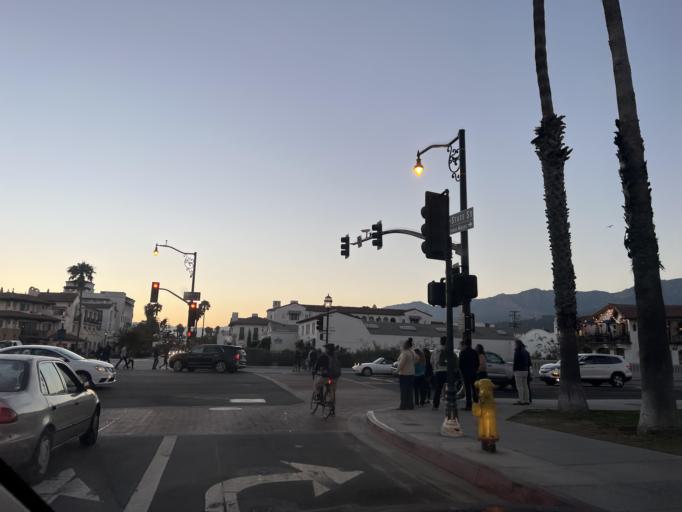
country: US
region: California
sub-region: Santa Barbara County
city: Santa Barbara
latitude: 34.4121
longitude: -119.6890
